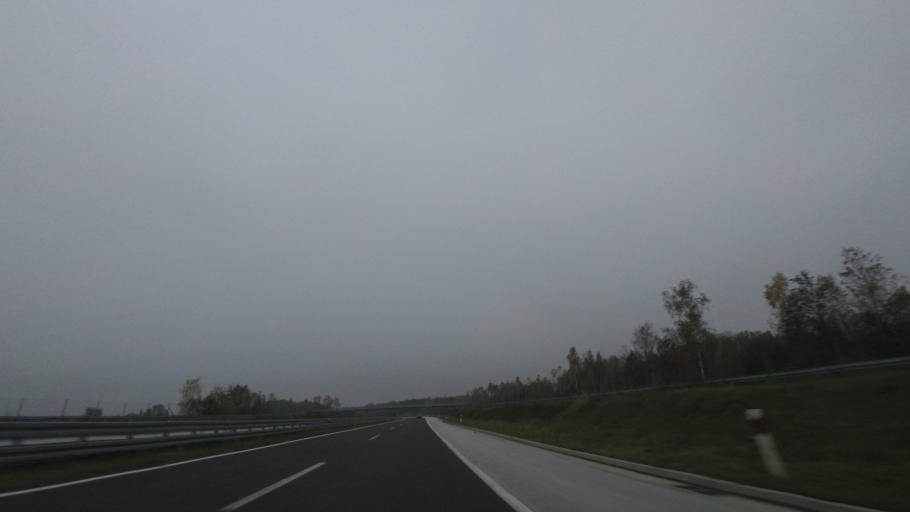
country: HR
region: Zagrebacka
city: Turopolje
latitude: 45.6101
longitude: 16.1187
